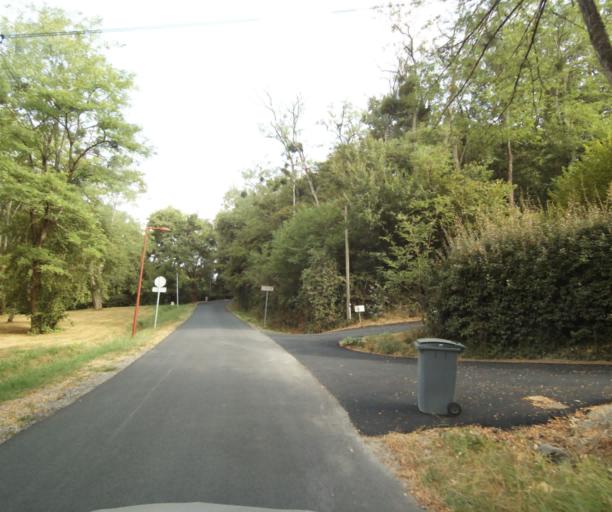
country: FR
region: Aquitaine
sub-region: Departement de la Gironde
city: Creon
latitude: 44.7612
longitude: -0.3523
